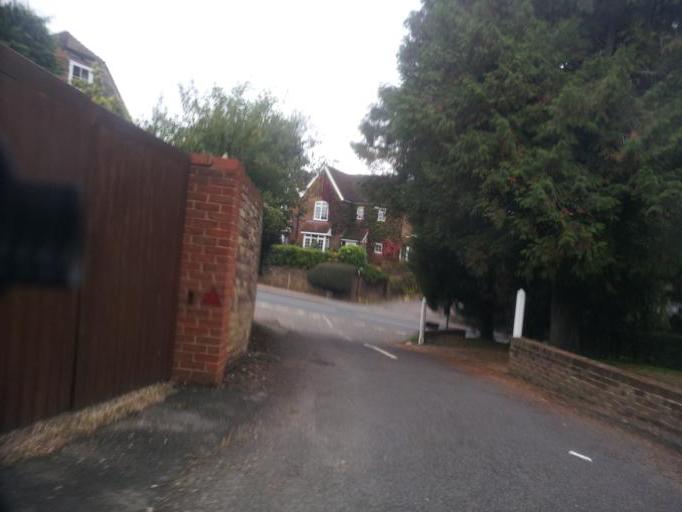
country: GB
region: England
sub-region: Kent
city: Teynham
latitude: 51.3262
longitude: 0.8052
